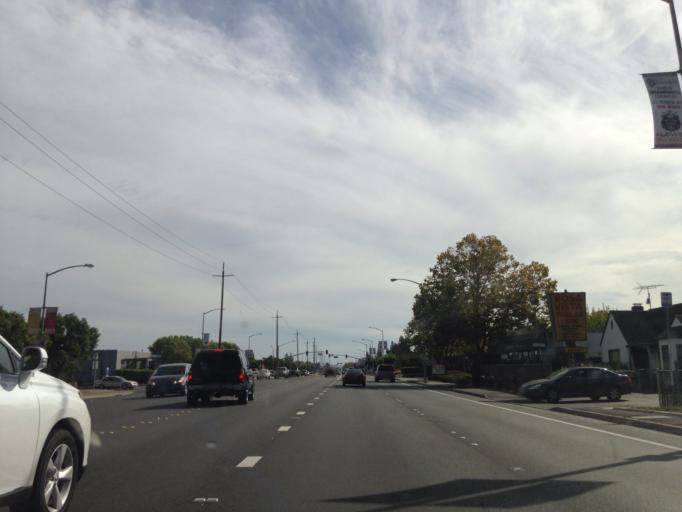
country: US
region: California
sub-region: Sonoma County
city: Roseland
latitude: 38.4206
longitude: -122.7136
